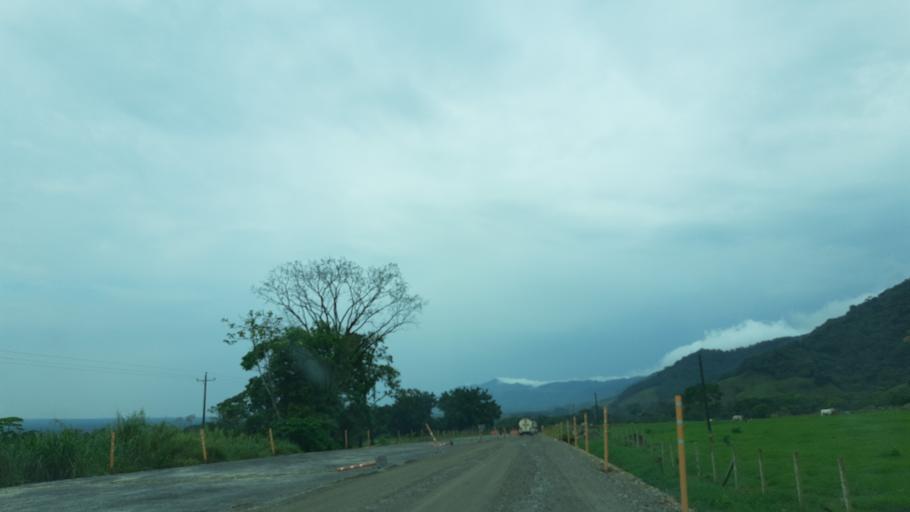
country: CO
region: Casanare
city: Monterrey
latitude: 4.8271
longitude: -72.9631
